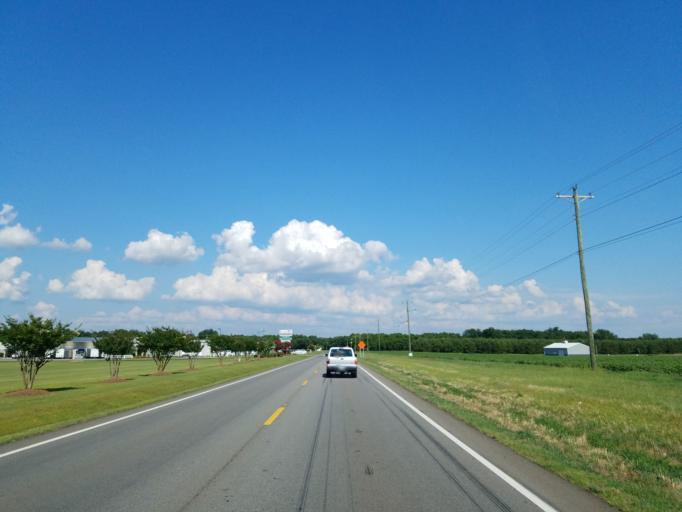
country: US
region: Georgia
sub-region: Peach County
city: Fort Valley
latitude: 32.5556
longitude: -83.8303
